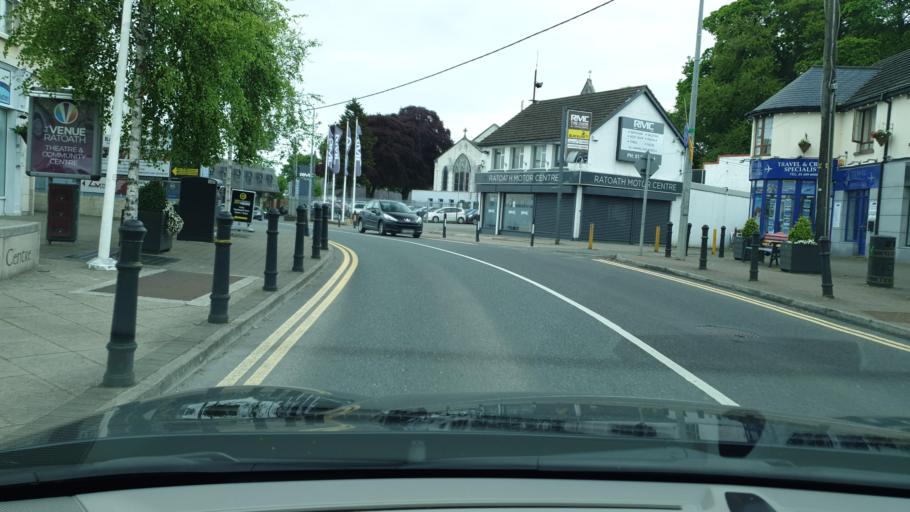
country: IE
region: Leinster
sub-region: An Mhi
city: Ratoath
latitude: 53.5073
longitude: -6.4630
